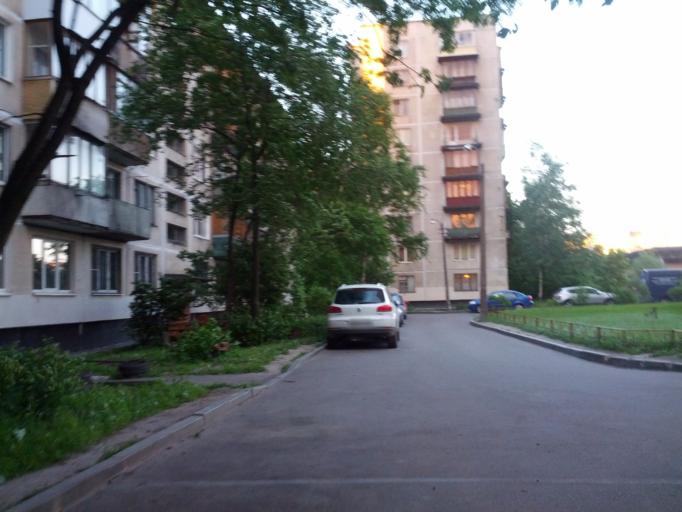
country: RU
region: St.-Petersburg
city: Obukhovo
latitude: 59.9061
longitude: 30.4696
